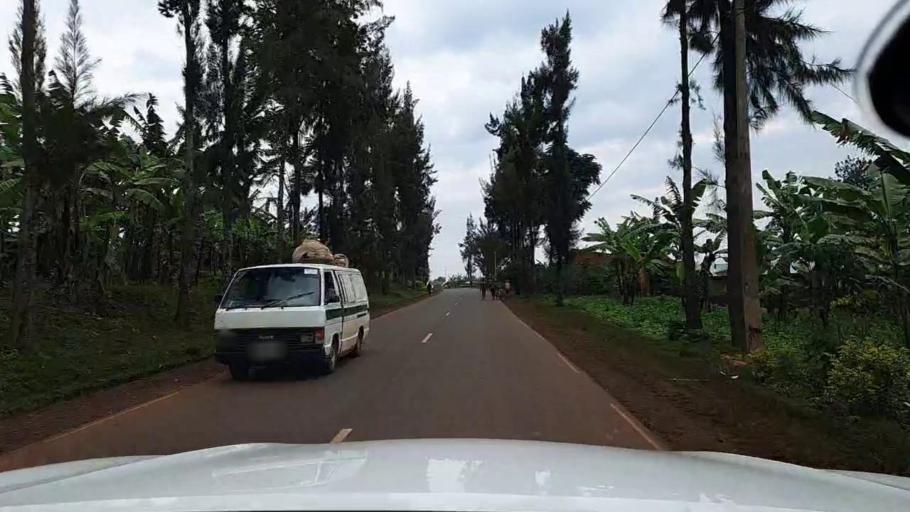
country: RW
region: Western Province
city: Cyangugu
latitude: -2.6168
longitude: 28.9446
